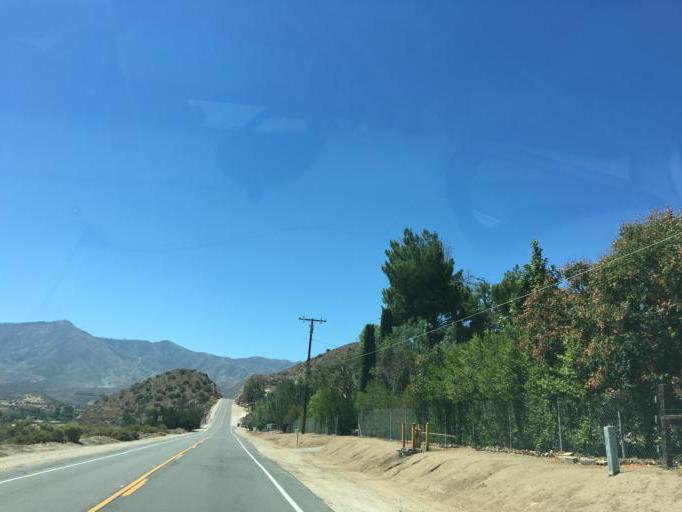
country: US
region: California
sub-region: Los Angeles County
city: Acton
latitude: 34.4628
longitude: -118.1977
